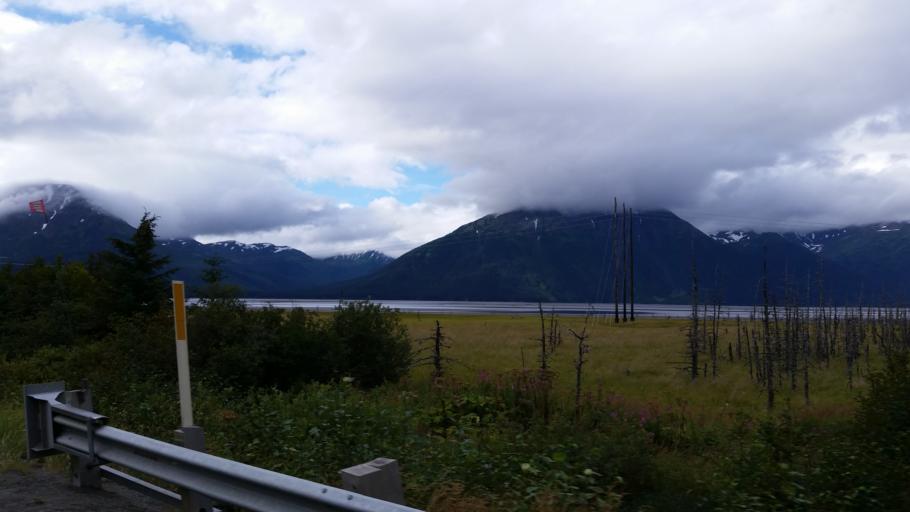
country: US
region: Alaska
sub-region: Anchorage Municipality
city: Girdwood
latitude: 60.9309
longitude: -149.1524
